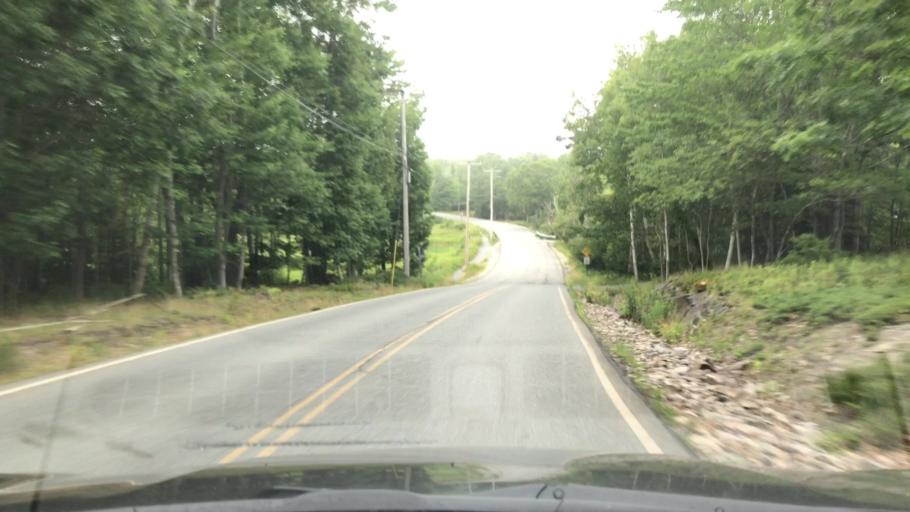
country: US
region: Maine
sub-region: Hancock County
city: Bar Harbor
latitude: 44.3416
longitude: -68.1803
